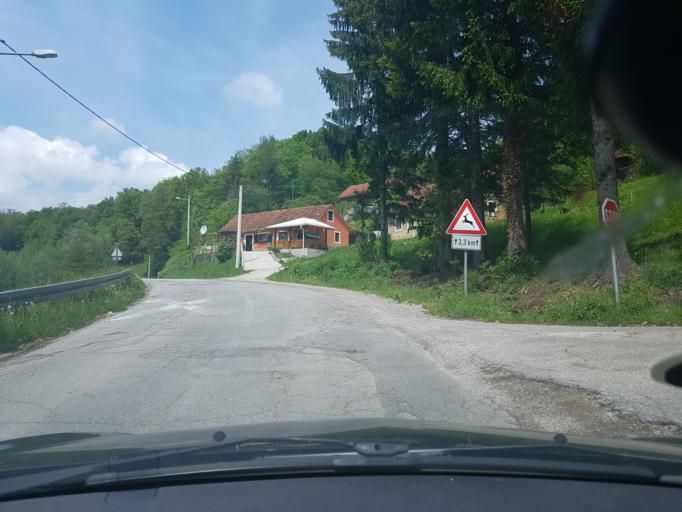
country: HR
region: Krapinsko-Zagorska
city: Pregrada
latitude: 46.1889
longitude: 15.7339
